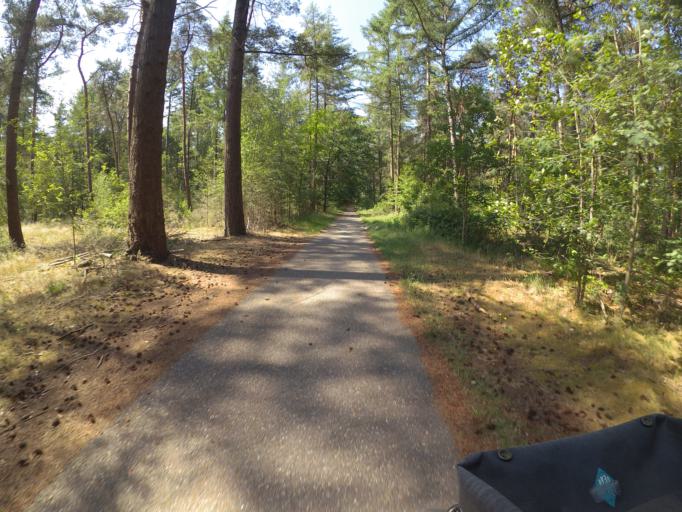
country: NL
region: North Brabant
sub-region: Gemeente Haaren
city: Haaren
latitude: 51.5662
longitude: 5.2280
